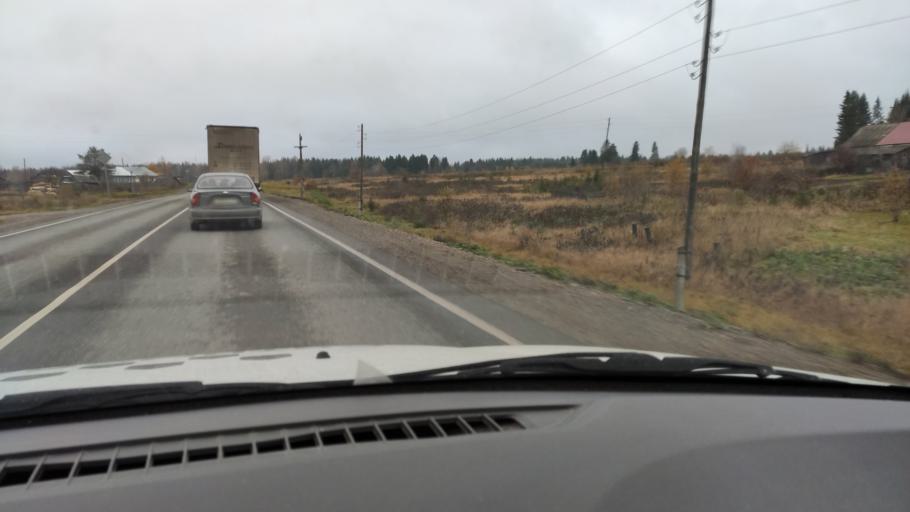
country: RU
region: Kirov
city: Omutninsk
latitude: 58.6921
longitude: 52.2084
